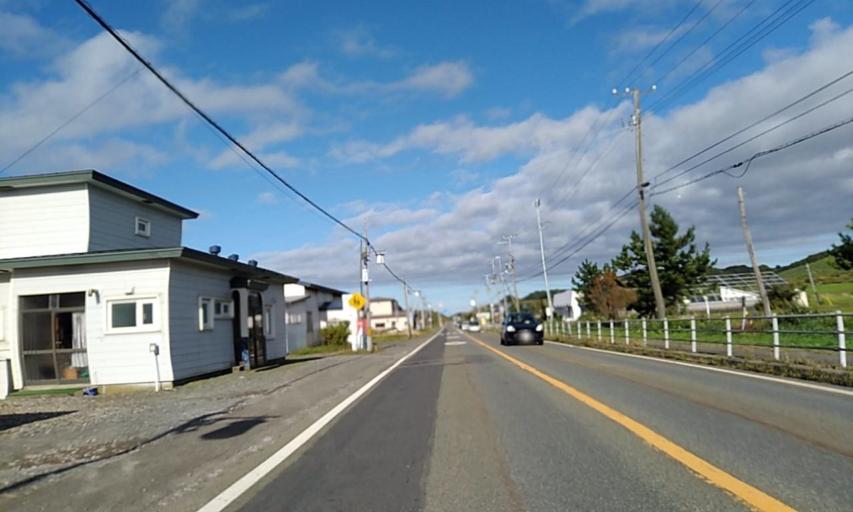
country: JP
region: Hokkaido
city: Shizunai-furukawacho
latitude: 42.2251
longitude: 142.6248
